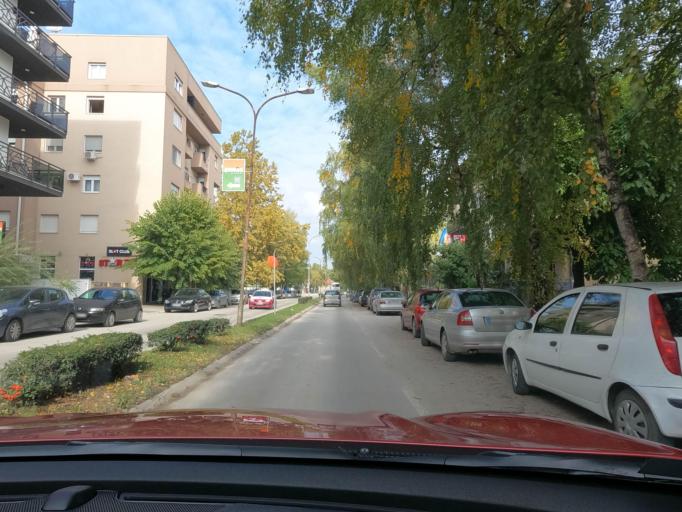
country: RS
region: Central Serbia
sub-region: Moravicki Okrug
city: Cacak
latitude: 43.8887
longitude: 20.3434
